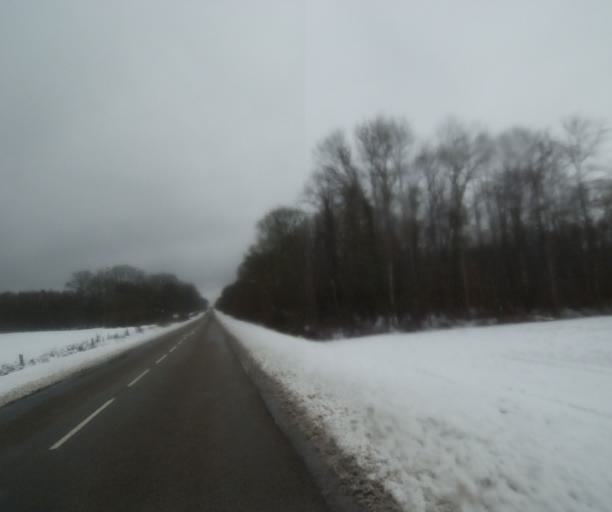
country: FR
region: Champagne-Ardenne
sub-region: Departement de la Haute-Marne
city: Montier-en-Der
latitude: 48.4811
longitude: 4.8034
